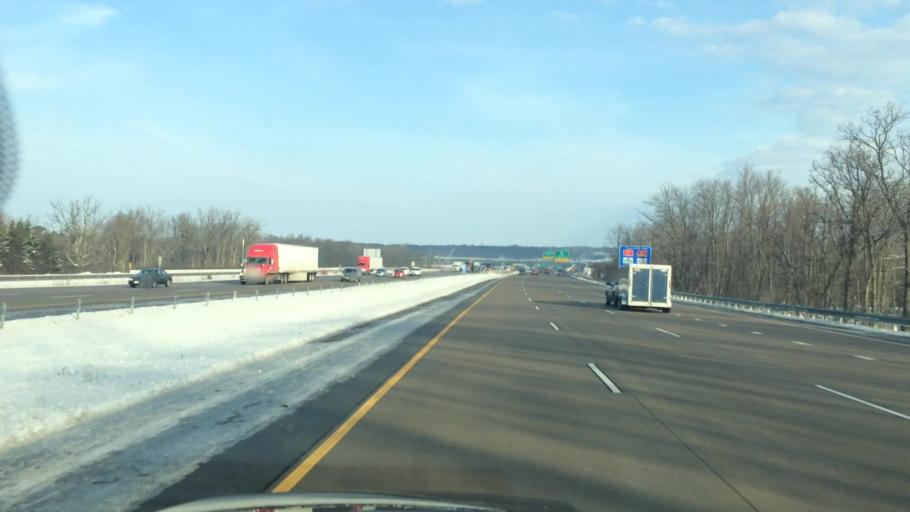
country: US
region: Wisconsin
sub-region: Marathon County
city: Rib Mountain
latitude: 44.9416
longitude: -89.6663
